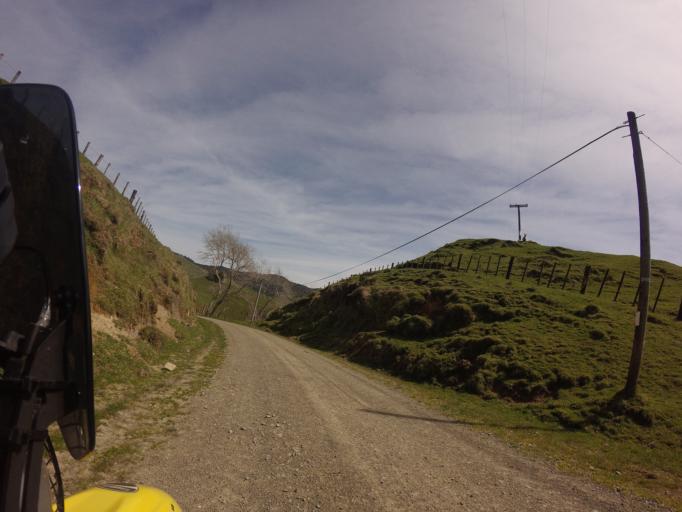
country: NZ
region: Bay of Plenty
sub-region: Opotiki District
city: Opotiki
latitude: -38.4532
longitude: 177.3571
